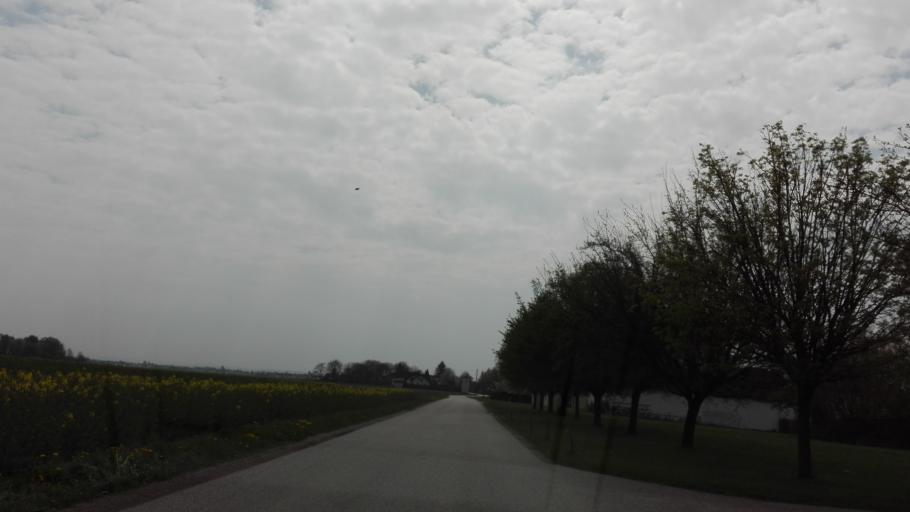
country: AT
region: Upper Austria
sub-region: Politischer Bezirk Perg
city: Perg
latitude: 48.2435
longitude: 14.5972
